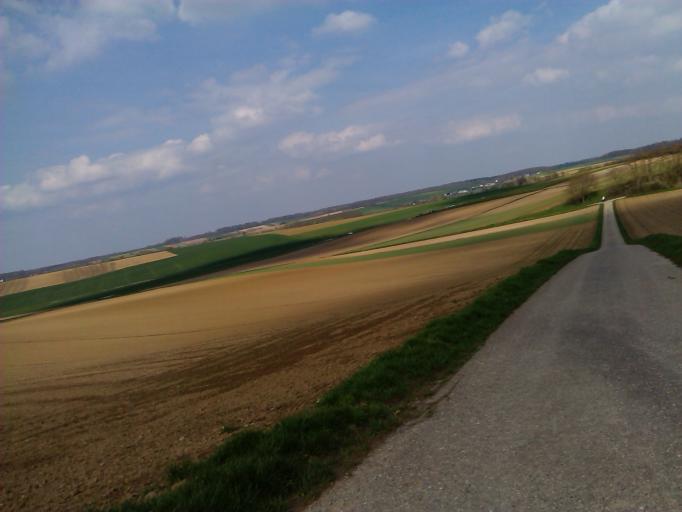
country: DE
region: Baden-Wuerttemberg
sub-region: Regierungsbezirk Stuttgart
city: Gemmingen
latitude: 49.1379
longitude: 8.9838
